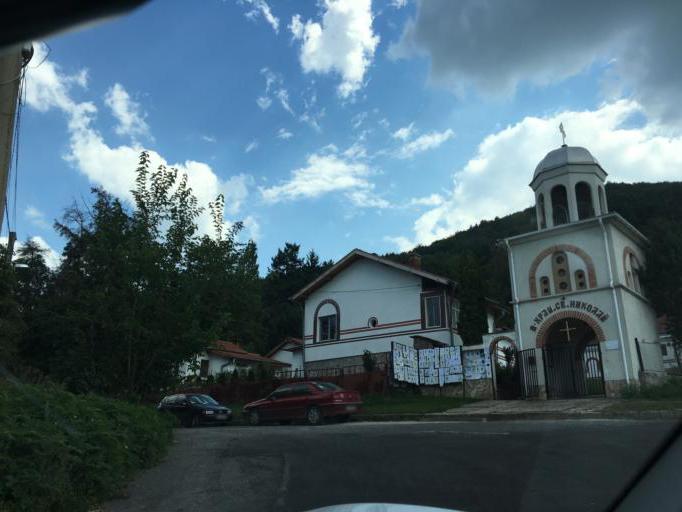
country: BG
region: Sofiya
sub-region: Obshtina Elin Pelin
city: Elin Pelin
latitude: 42.5987
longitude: 23.4781
